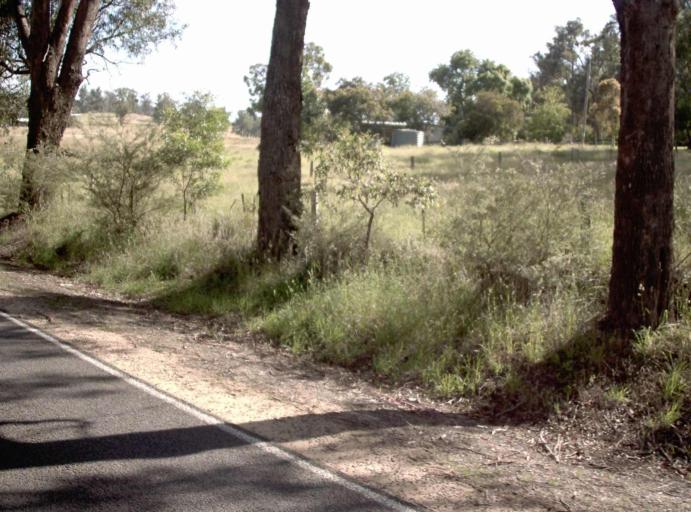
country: AU
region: Victoria
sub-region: East Gippsland
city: Lakes Entrance
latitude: -37.5417
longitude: 148.1484
